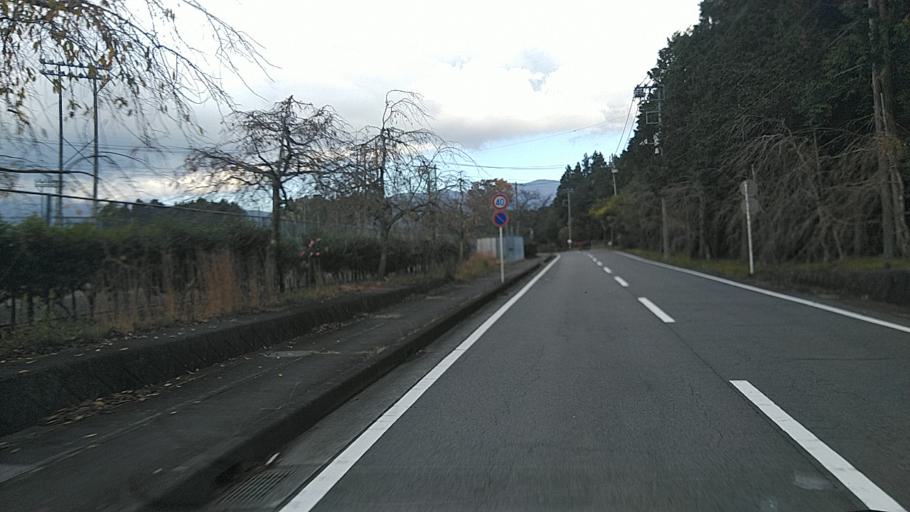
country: JP
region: Shizuoka
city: Gotemba
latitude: 35.3199
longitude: 138.9587
